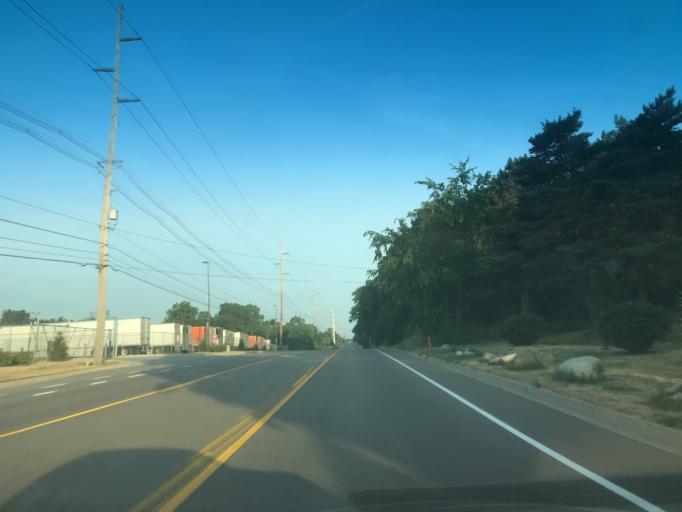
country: US
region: Michigan
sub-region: Eaton County
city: Waverly
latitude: 42.7121
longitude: -84.6470
